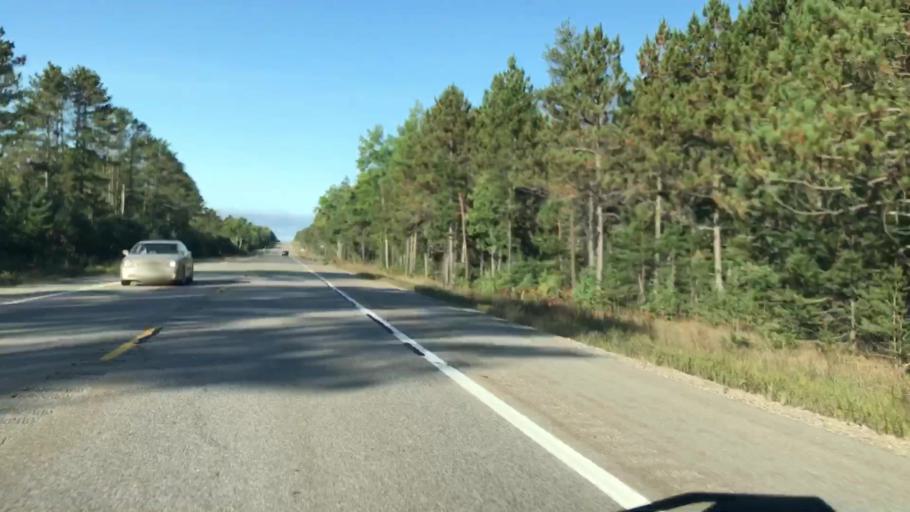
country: US
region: Michigan
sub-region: Chippewa County
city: Sault Ste. Marie
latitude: 46.3670
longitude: -84.7510
